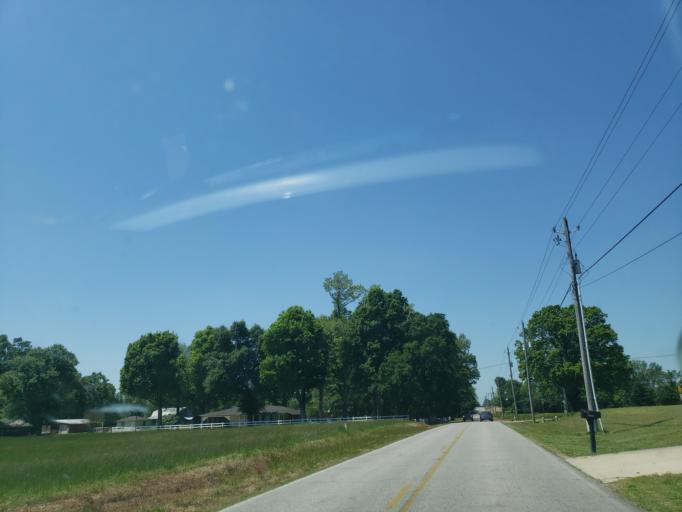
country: US
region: Alabama
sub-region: Madison County
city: Harvest
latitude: 34.9625
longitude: -86.7186
